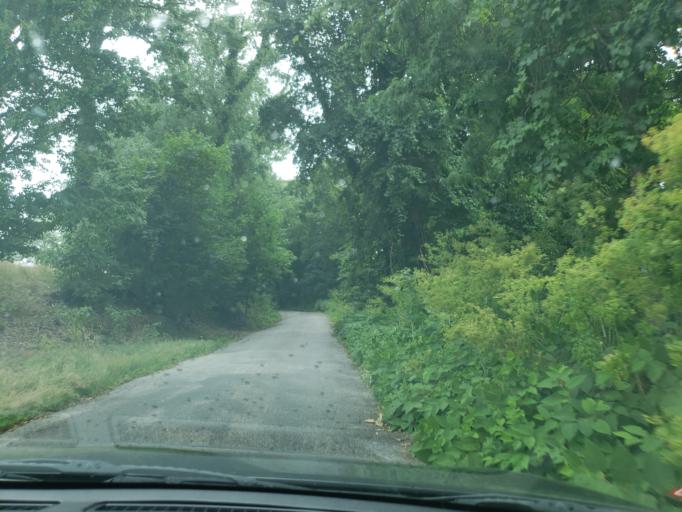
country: US
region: Pennsylvania
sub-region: Allegheny County
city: Avalon
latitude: 40.5152
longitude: -80.0649
